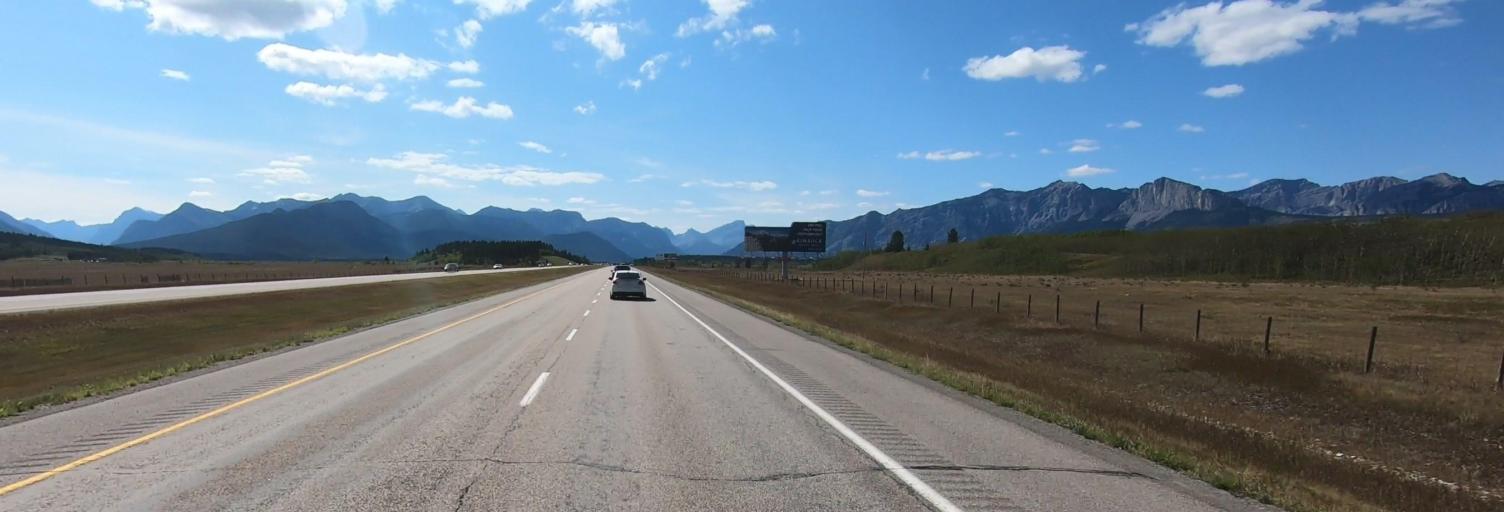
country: CA
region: Alberta
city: Canmore
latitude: 51.1169
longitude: -114.9828
